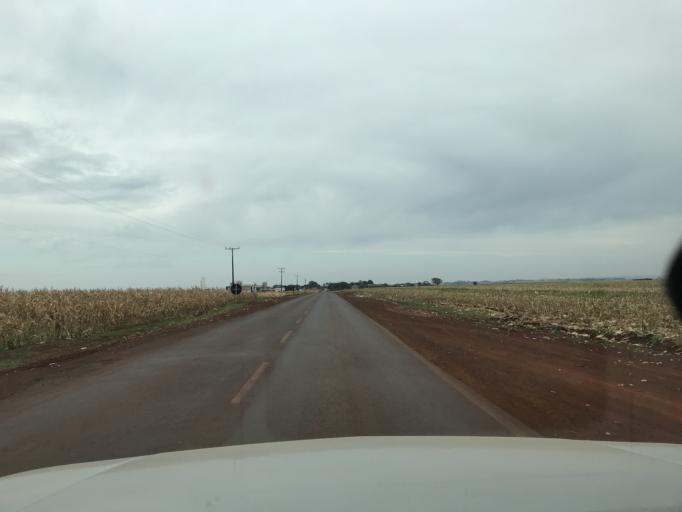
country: BR
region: Parana
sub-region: Palotina
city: Palotina
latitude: -24.4189
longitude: -53.8690
